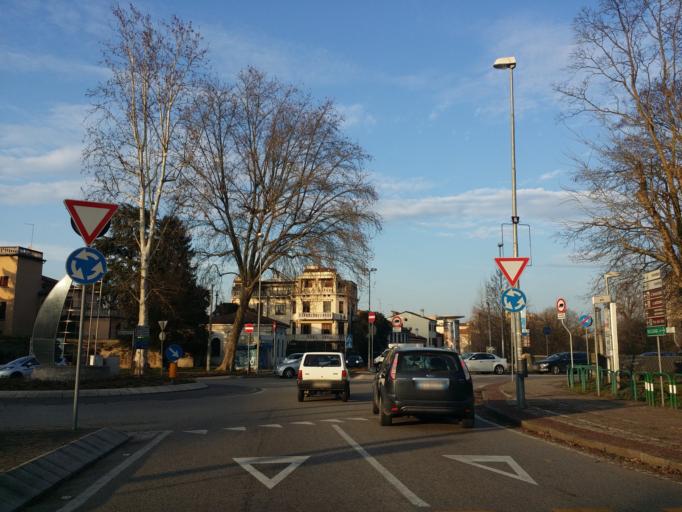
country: IT
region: Veneto
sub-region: Provincia di Padova
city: Padova
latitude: 45.3989
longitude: 11.8646
